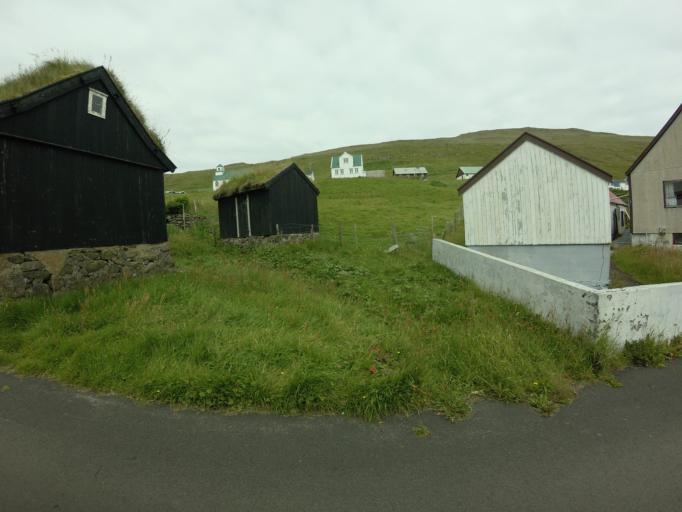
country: FO
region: Suduroy
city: Tvoroyri
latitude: 61.6328
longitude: -6.9282
